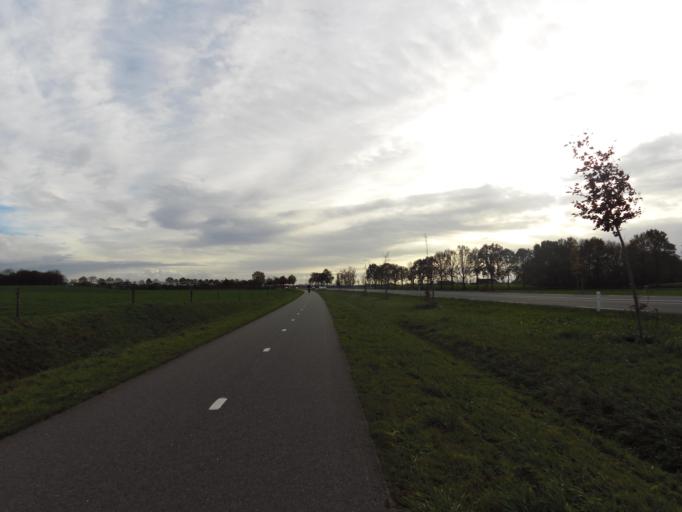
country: NL
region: Gelderland
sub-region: Gemeente Doetinchem
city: Doetinchem
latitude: 51.9314
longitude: 6.3154
